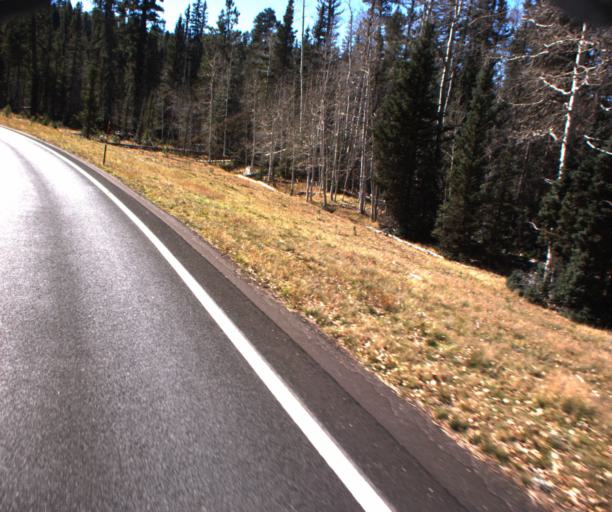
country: US
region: Arizona
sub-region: Coconino County
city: Grand Canyon
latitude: 36.4517
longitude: -112.1351
